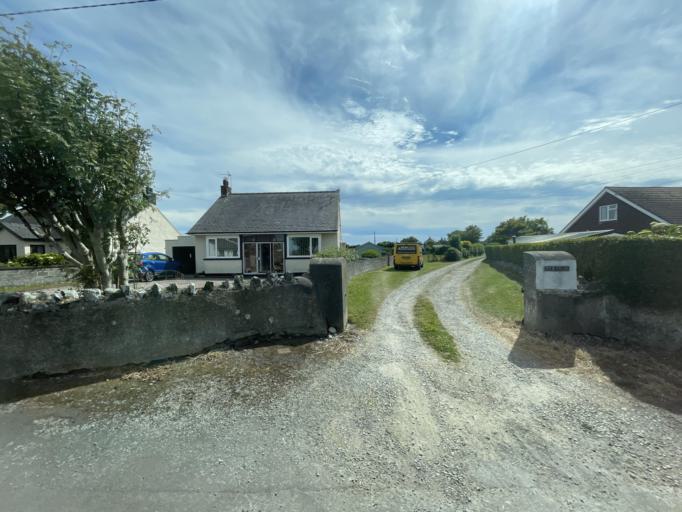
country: GB
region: Wales
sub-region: Anglesey
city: Valley
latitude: 53.2747
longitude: -4.6055
